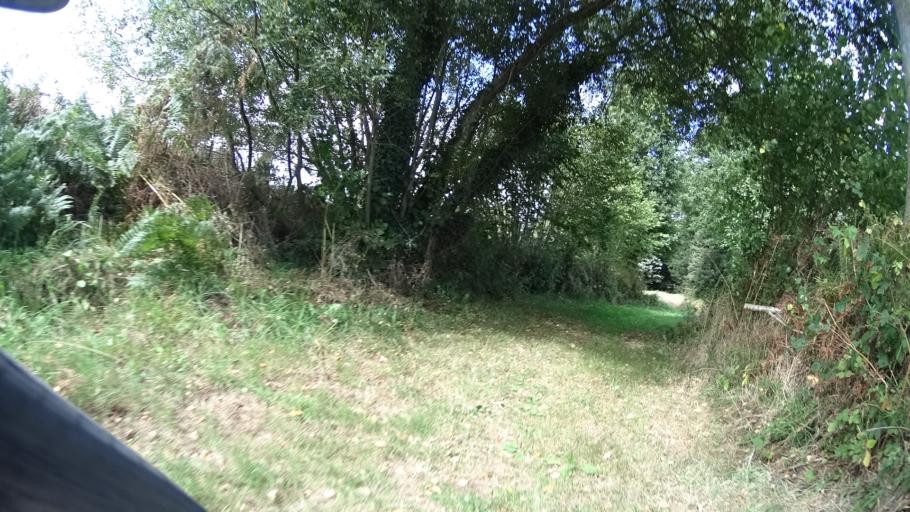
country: FR
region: Brittany
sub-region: Departement d'Ille-et-Vilaine
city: La Meziere
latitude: 48.2186
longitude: -1.7365
